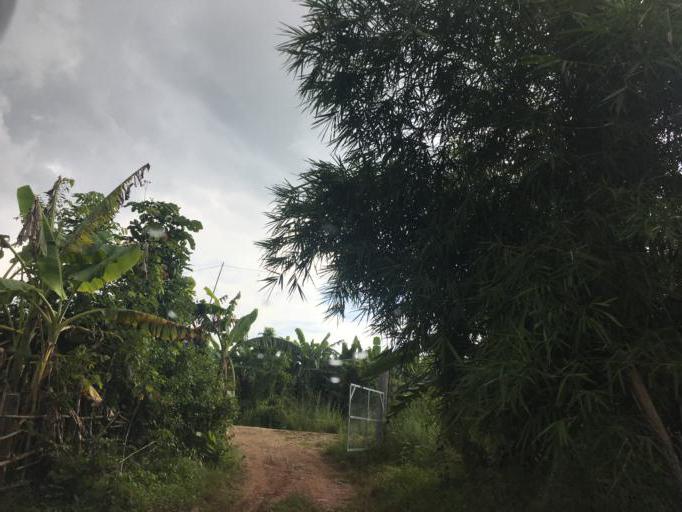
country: TH
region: Nong Khai
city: Sangkhom
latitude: 18.1457
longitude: 102.2688
